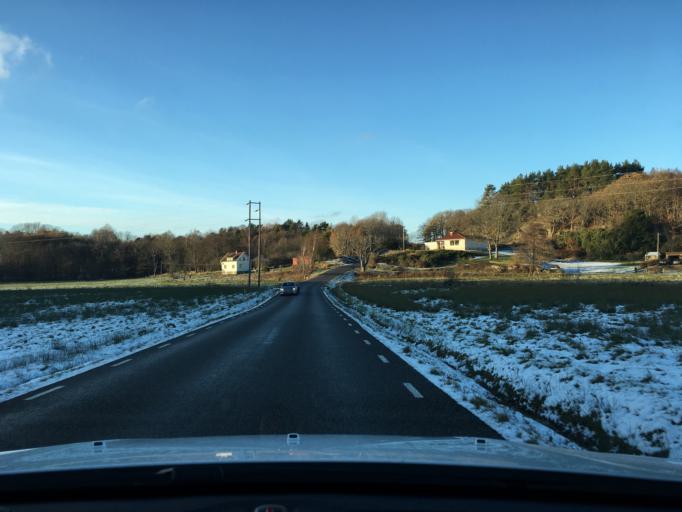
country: SE
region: Vaestra Goetaland
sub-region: Tjorns Kommun
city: Myggenas
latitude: 58.0550
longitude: 11.6969
